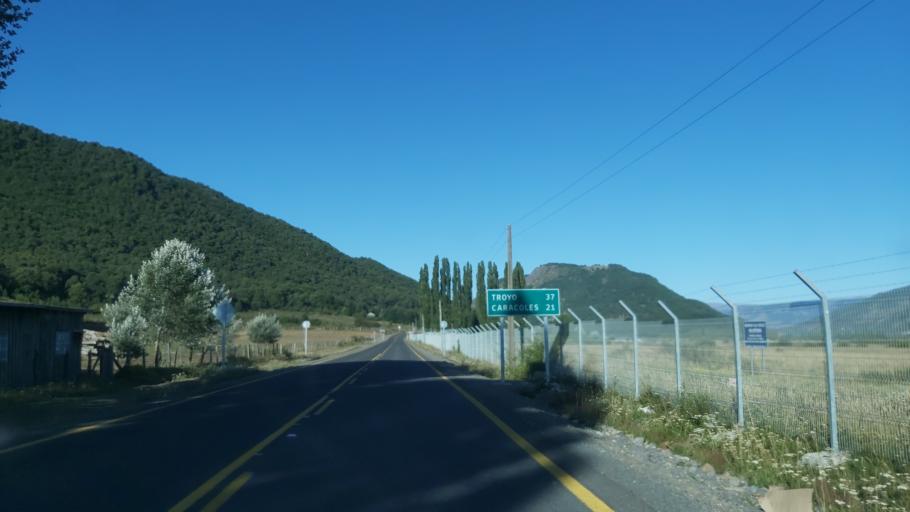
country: AR
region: Neuquen
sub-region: Departamento de Loncopue
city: Loncopue
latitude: -38.4479
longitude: -71.3624
